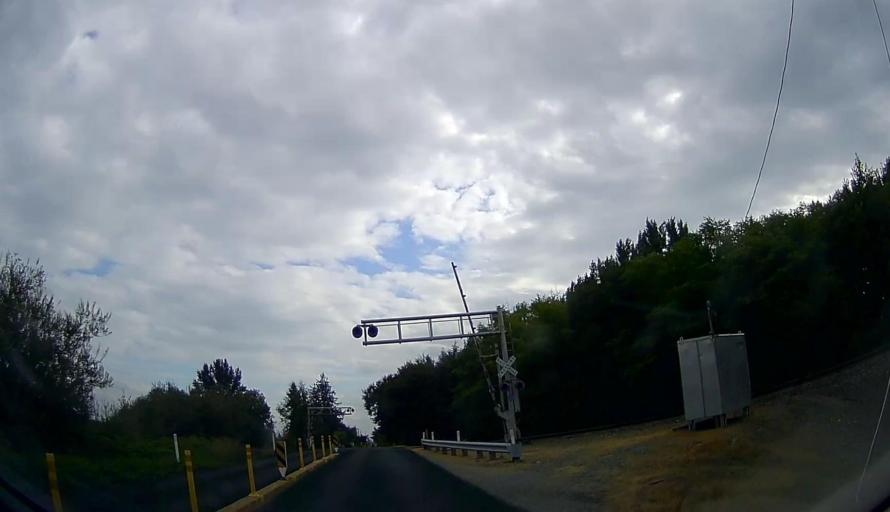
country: US
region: Washington
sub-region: Skagit County
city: Burlington
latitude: 48.5910
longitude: -122.4166
